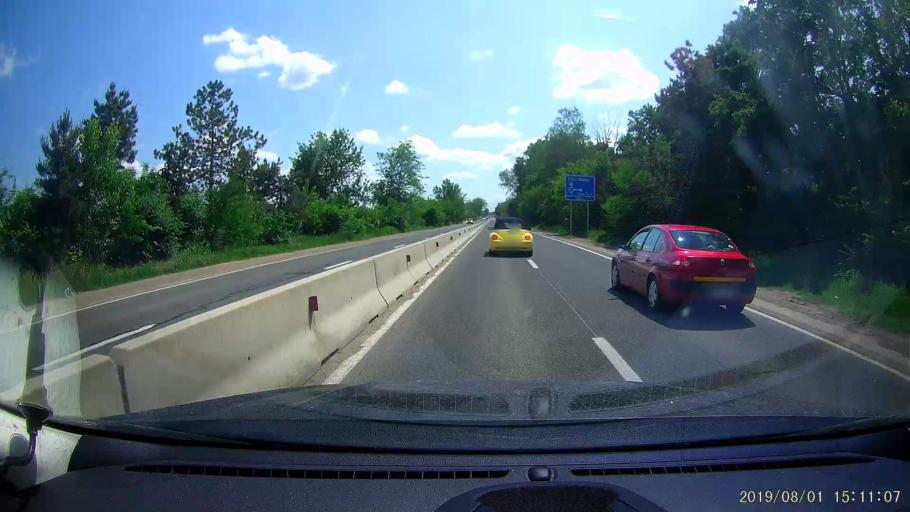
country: RO
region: Braila
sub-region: Comuna Chiscani
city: Chiscani
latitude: 45.2206
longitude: 27.9267
